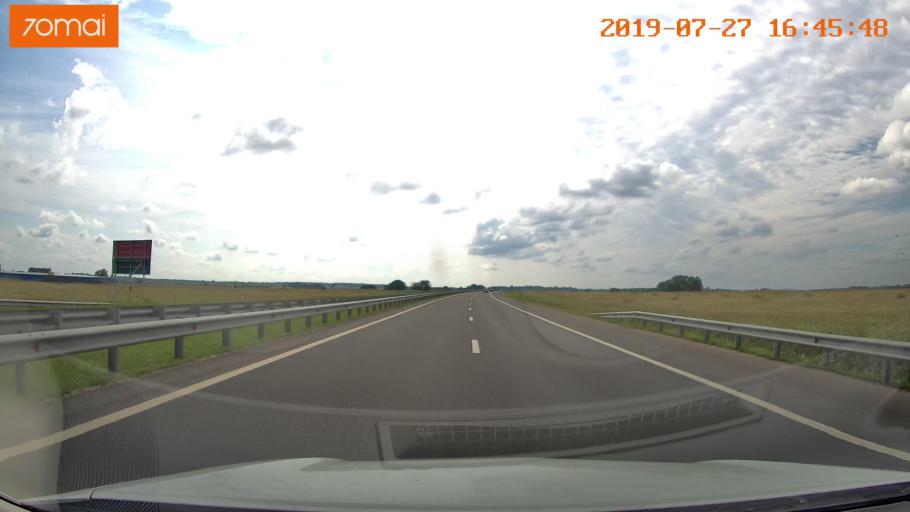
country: RU
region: Kaliningrad
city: Gvardeysk
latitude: 54.6683
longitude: 21.0400
